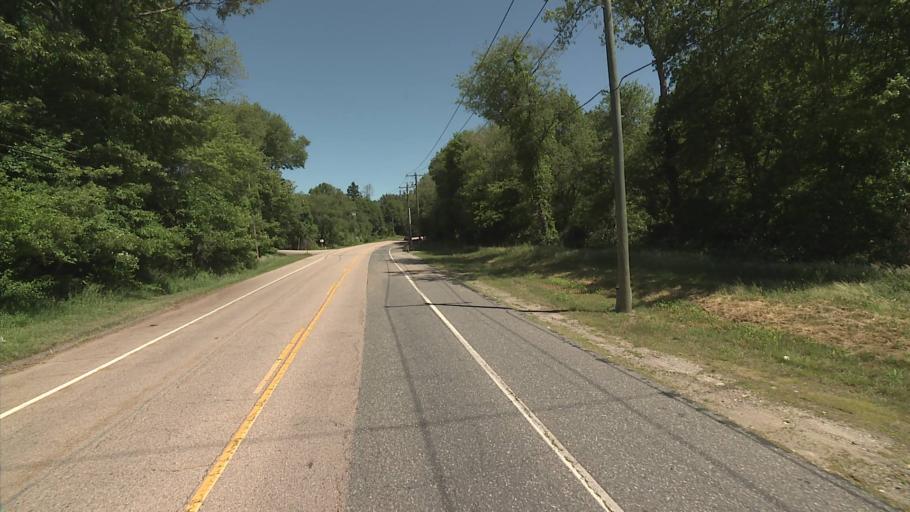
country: US
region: Connecticut
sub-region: New London County
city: Pawcatuck
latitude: 41.4126
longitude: -71.8453
